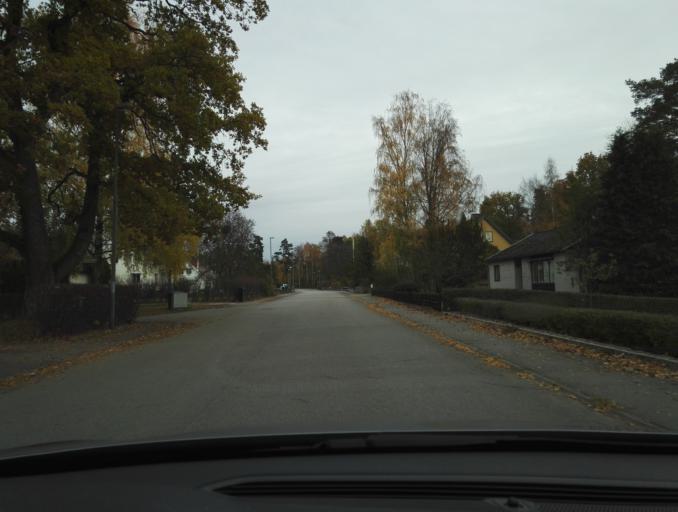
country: SE
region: Kronoberg
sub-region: Vaxjo Kommun
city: Vaexjoe
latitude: 56.9115
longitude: 14.7470
